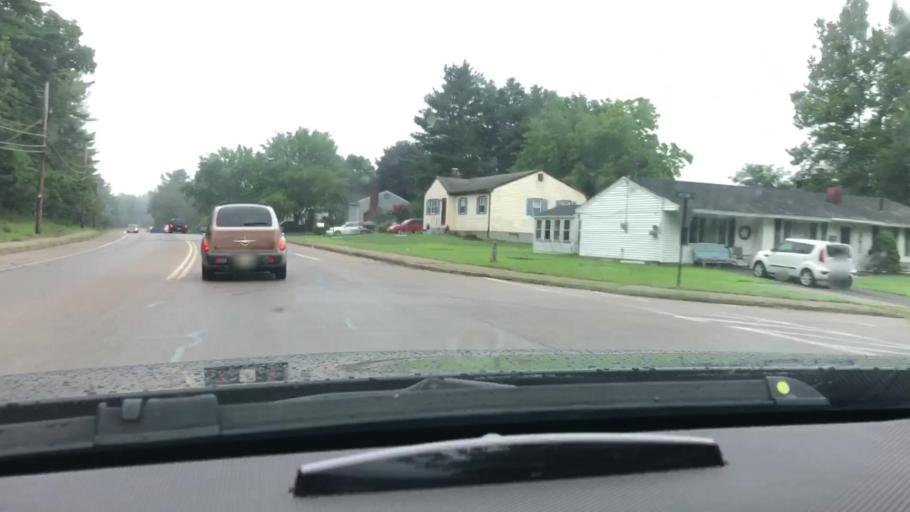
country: US
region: Massachusetts
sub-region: Norfolk County
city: Bellingham
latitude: 42.1071
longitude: -71.4740
